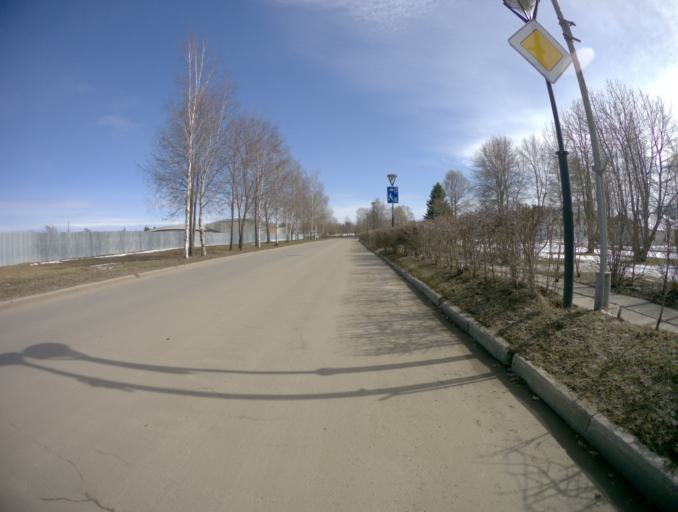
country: RU
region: Vladimir
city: Suzdal'
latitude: 56.4318
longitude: 40.4222
